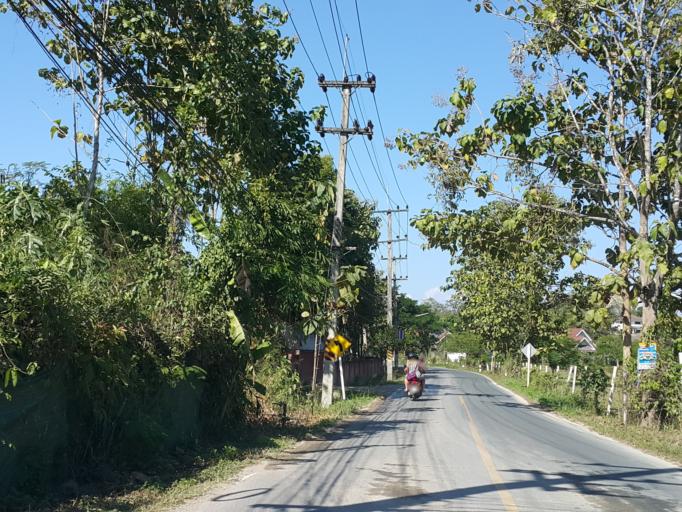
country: TH
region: Chiang Mai
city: San Sai
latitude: 18.9415
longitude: 98.9295
